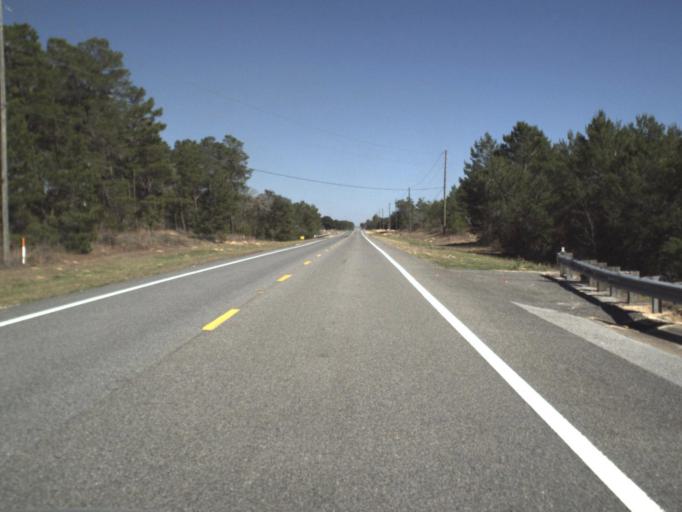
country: US
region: Florida
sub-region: Bay County
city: Lynn Haven
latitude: 30.4246
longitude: -85.6427
